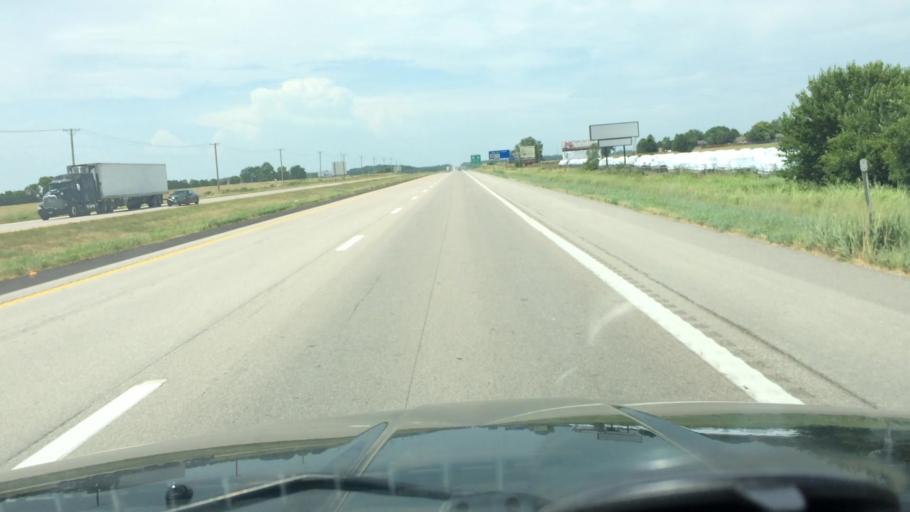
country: US
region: Missouri
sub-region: Polk County
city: Bolivar
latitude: 37.6001
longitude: -93.4378
